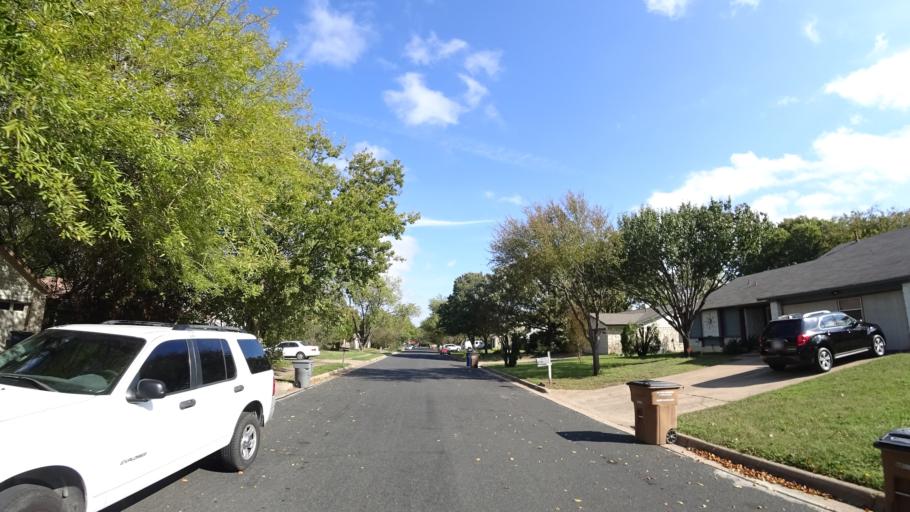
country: US
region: Texas
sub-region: Travis County
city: Shady Hollow
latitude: 30.1934
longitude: -97.8241
